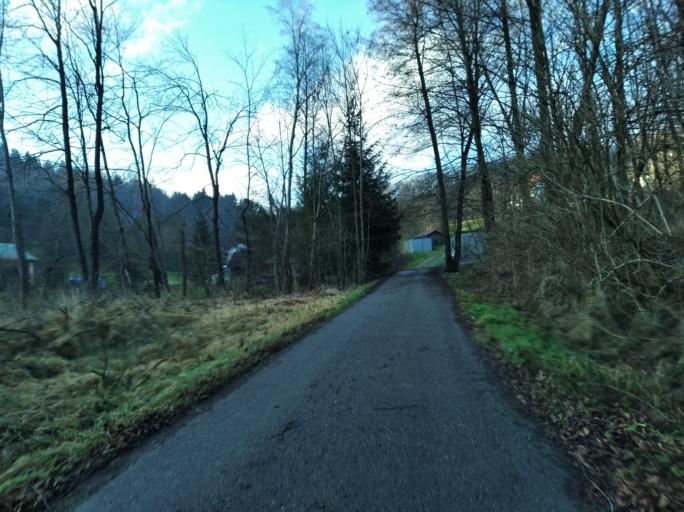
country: PL
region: Subcarpathian Voivodeship
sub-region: Powiat strzyzowski
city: Czudec
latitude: 49.9512
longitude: 21.7941
